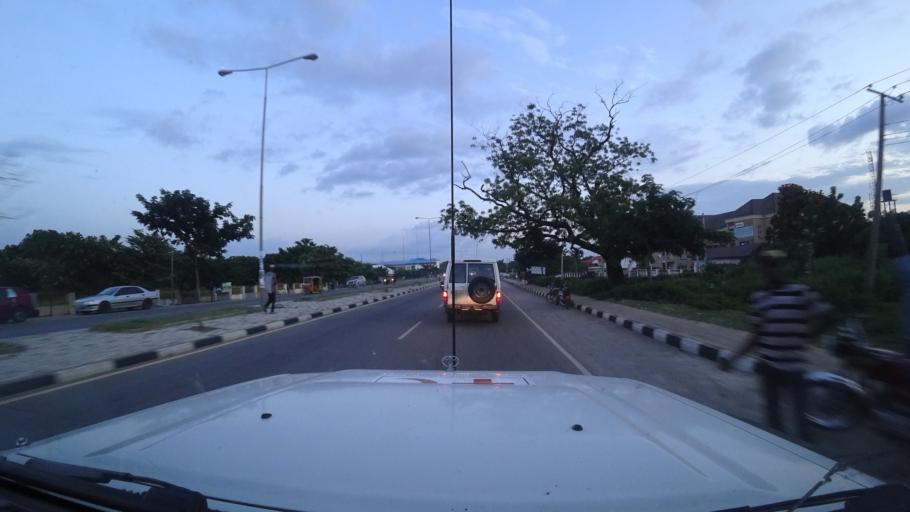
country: NG
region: Niger
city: Minna
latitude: 9.6351
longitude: 6.5431
